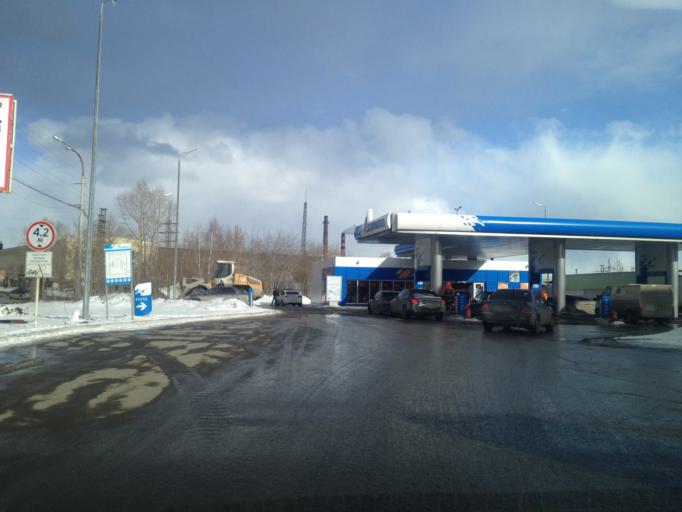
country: RU
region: Sverdlovsk
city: Yekaterinburg
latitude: 56.8780
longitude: 60.6218
